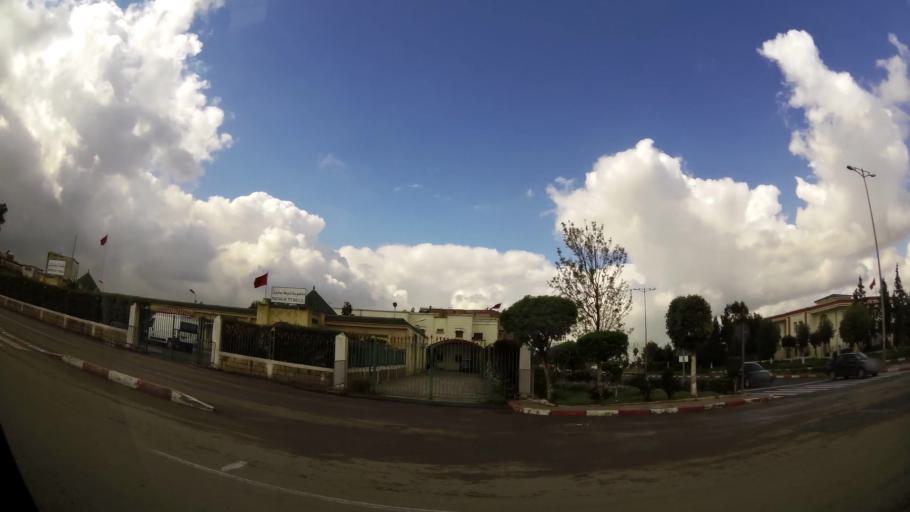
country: MA
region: Grand Casablanca
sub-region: Mediouna
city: Tit Mellil
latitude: 33.5565
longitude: -7.4840
